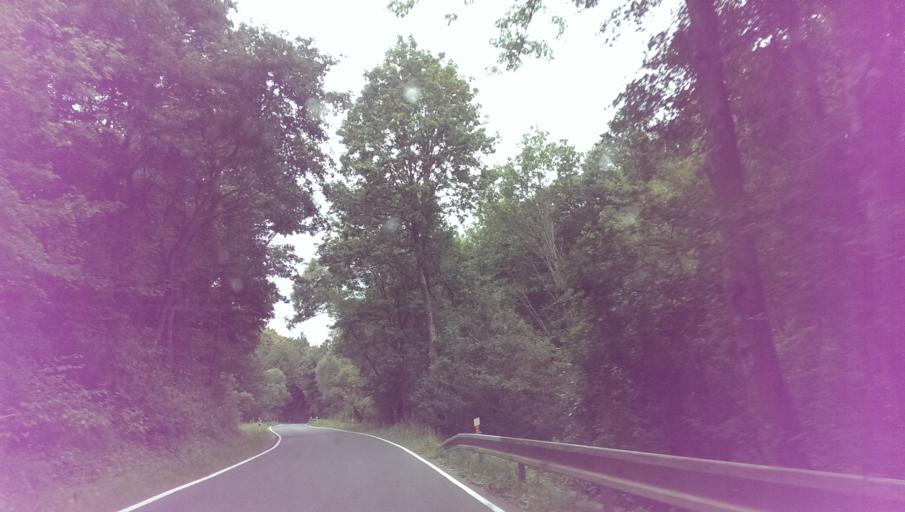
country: CZ
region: South Moravian
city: Velka nad Velickou
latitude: 48.8751
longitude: 17.5878
